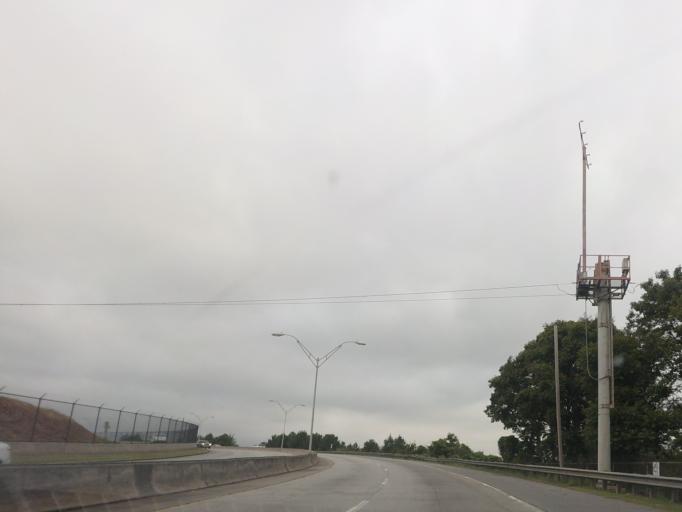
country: US
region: Georgia
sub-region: Fulton County
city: Hapeville
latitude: 33.6467
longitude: -84.4009
